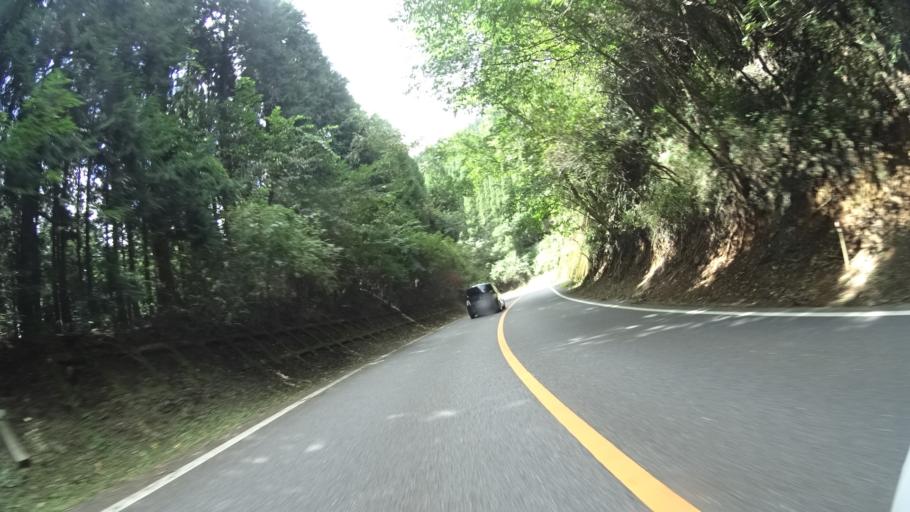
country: JP
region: Oita
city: Tsukawaki
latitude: 33.2224
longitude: 131.2988
